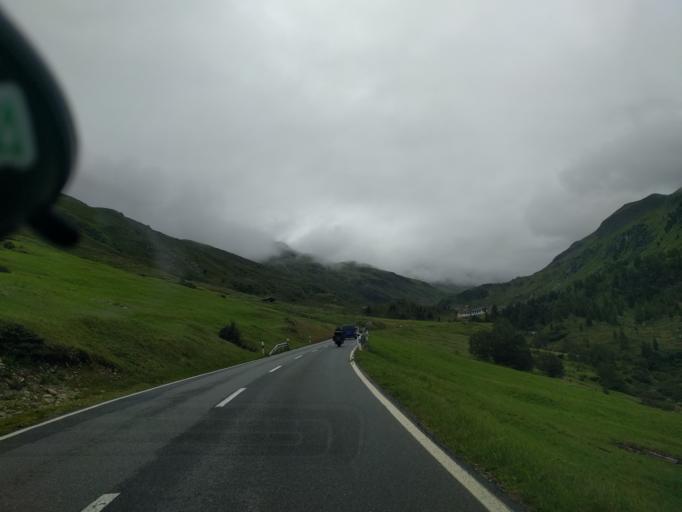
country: CH
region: Grisons
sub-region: Praettigau/Davos District
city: Davos
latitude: 46.7926
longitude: 9.9128
